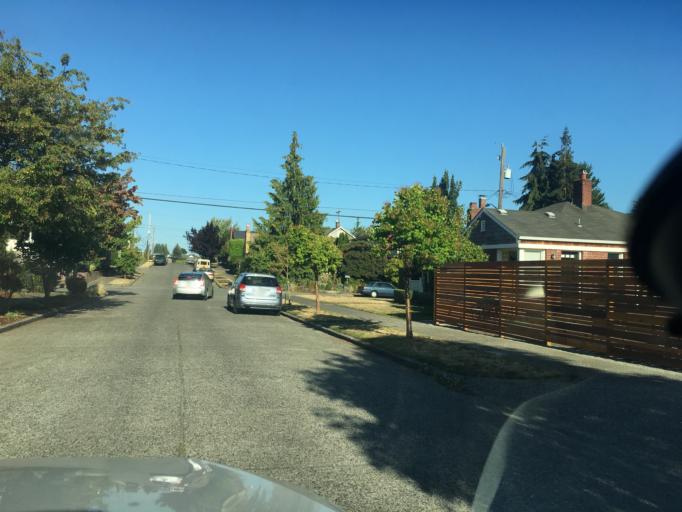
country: US
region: Washington
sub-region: King County
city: Shoreline
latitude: 47.6890
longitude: -122.3904
